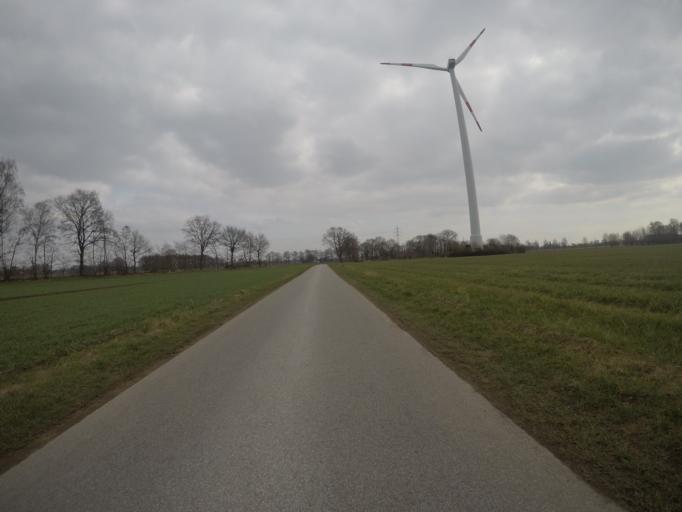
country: DE
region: North Rhine-Westphalia
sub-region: Regierungsbezirk Dusseldorf
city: Hamminkeln
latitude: 51.7853
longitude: 6.5821
